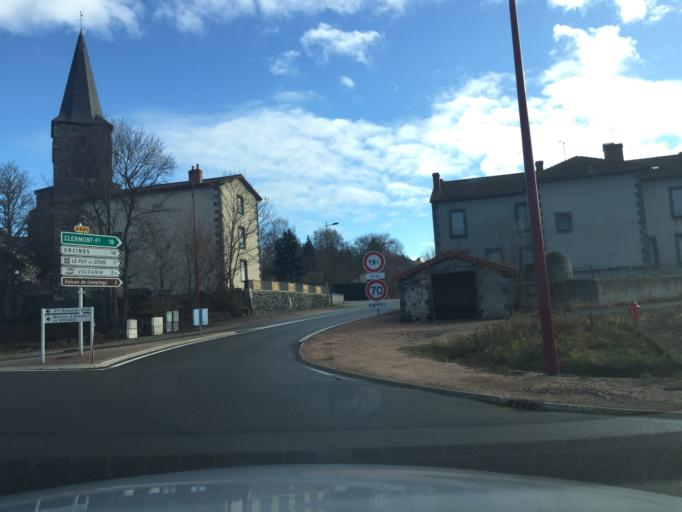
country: FR
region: Auvergne
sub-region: Departement du Puy-de-Dome
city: Saint-Ours
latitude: 45.8241
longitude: 2.9120
